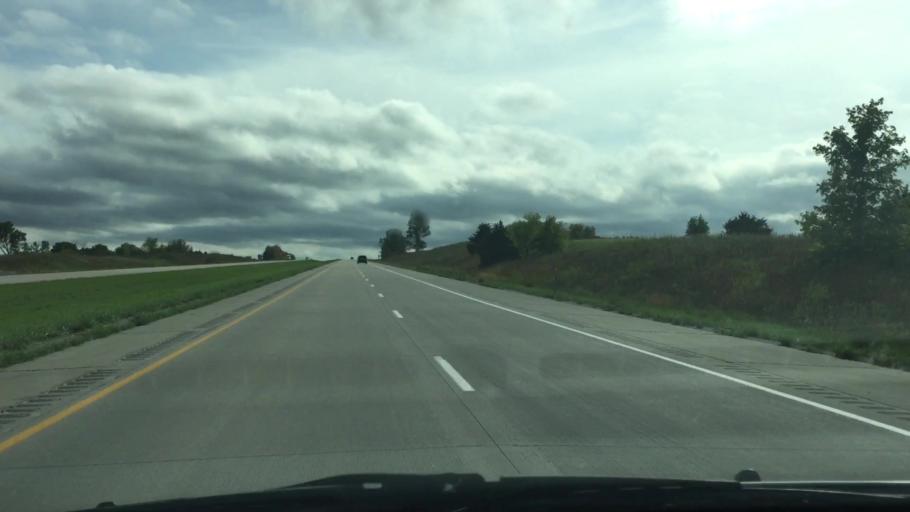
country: US
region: Iowa
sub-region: Decatur County
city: Leon
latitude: 40.7869
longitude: -93.8352
